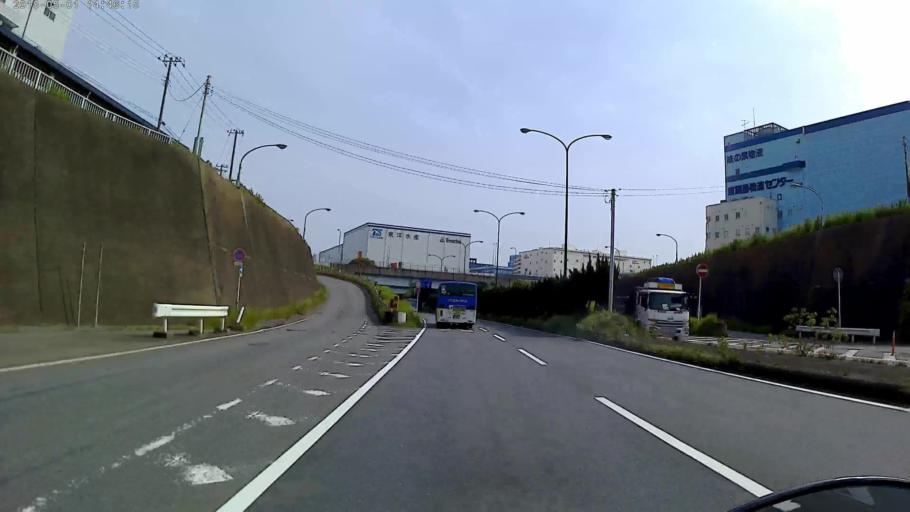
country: JP
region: Kanagawa
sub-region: Kawasaki-shi
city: Kawasaki
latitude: 35.5008
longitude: 139.7600
